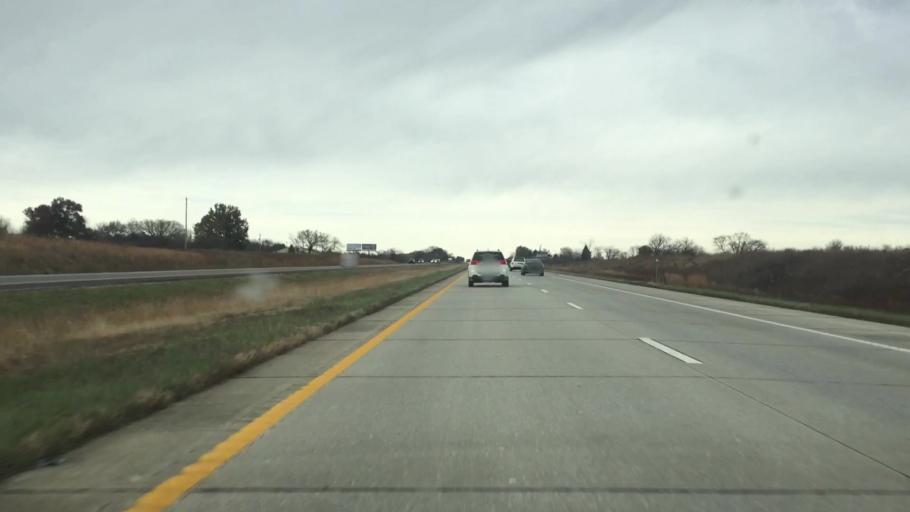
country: US
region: Missouri
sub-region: Saint Clair County
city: Osceola
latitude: 38.0899
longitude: -93.7074
